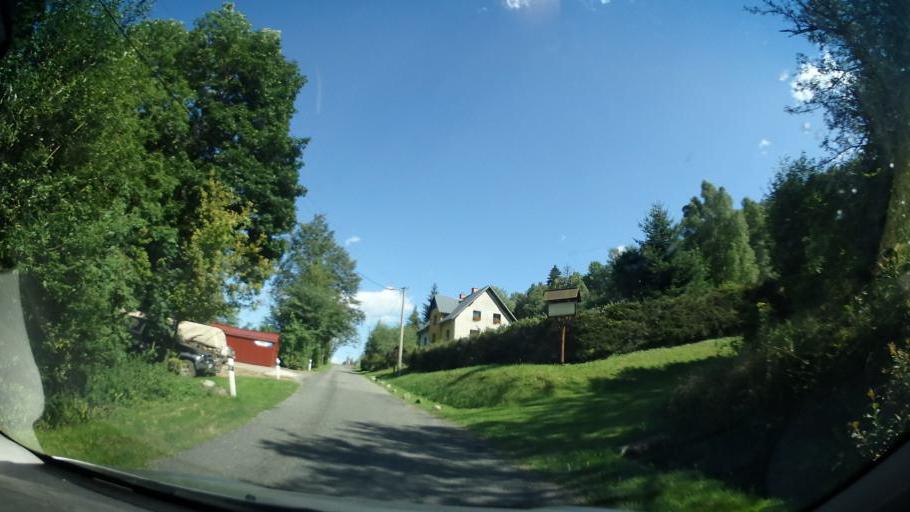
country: CZ
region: Olomoucky
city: Vapenna
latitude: 50.2253
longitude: 17.0802
